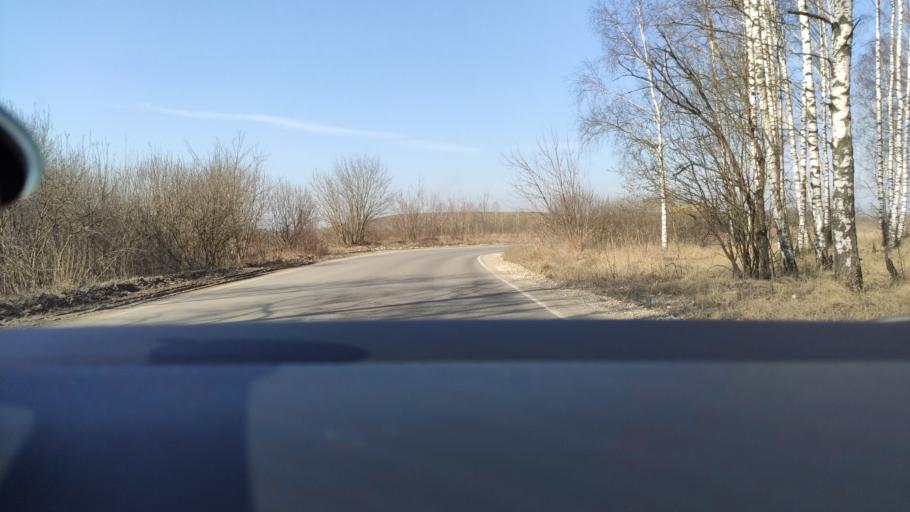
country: RU
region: Moskovskaya
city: Elektrostal'
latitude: 55.7641
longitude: 38.3883
